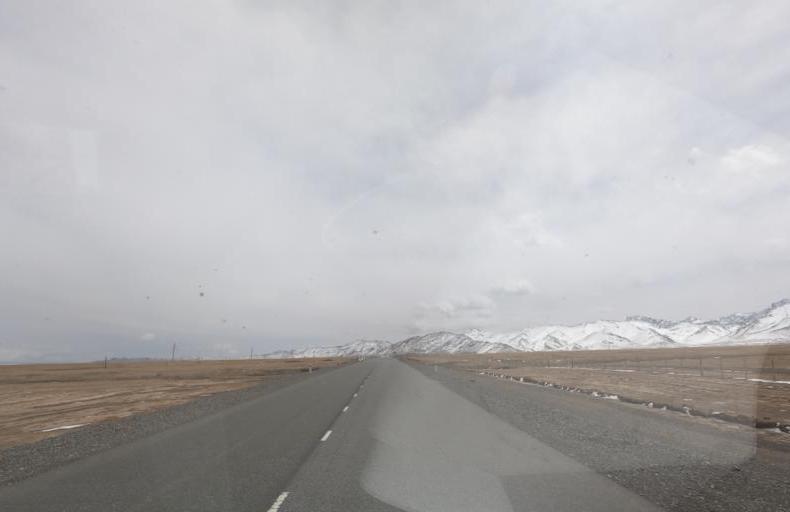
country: KG
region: Naryn
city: Baetov
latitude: 40.5531
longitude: 75.2094
